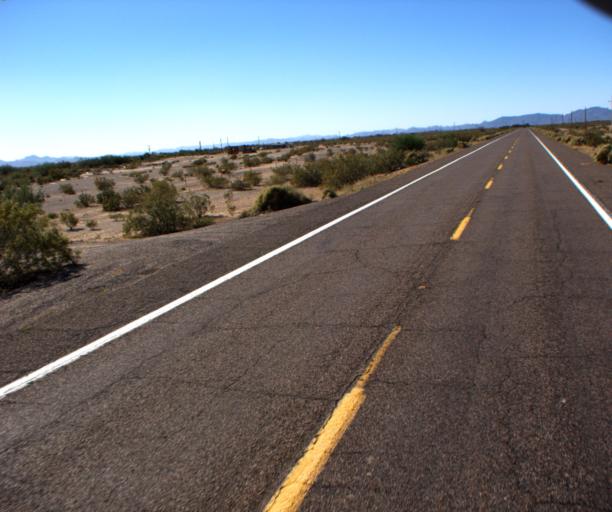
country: US
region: Arizona
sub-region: Maricopa County
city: Gila Bend
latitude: 32.9232
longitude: -112.7346
